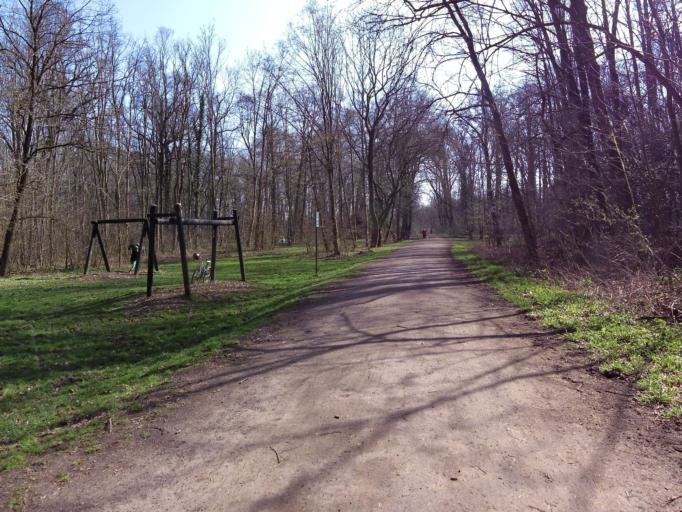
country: DE
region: Saxony
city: Leipzig
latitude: 51.3645
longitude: 12.2964
